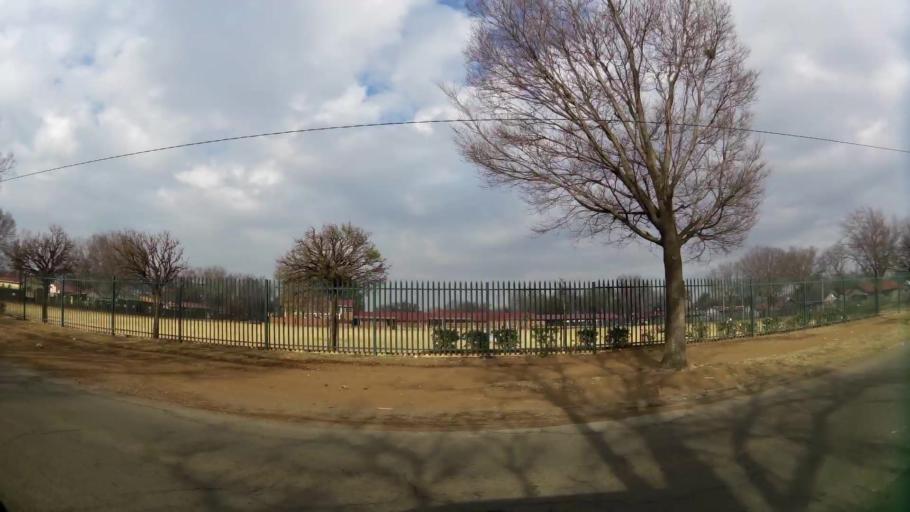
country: ZA
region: Gauteng
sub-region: Sedibeng District Municipality
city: Vanderbijlpark
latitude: -26.7044
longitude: 27.8177
